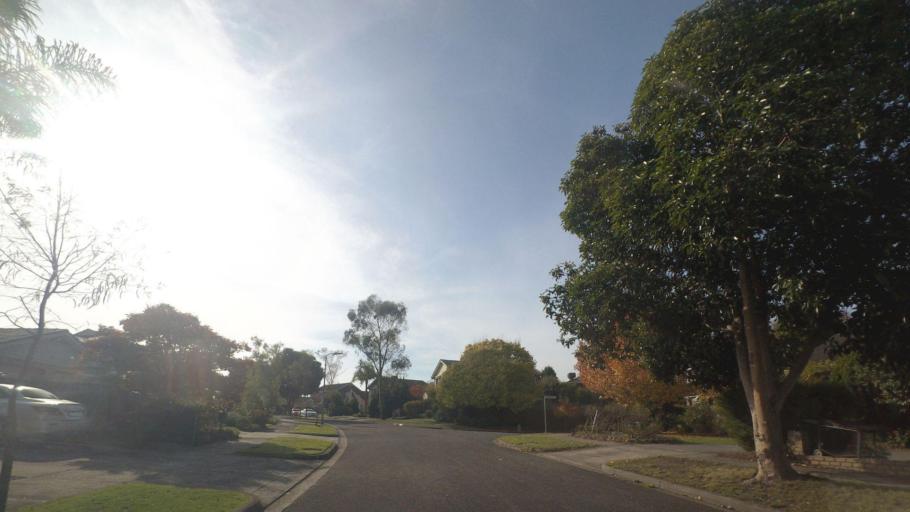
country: AU
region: Victoria
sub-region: Manningham
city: Doncaster East
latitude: -37.7764
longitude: 145.1508
